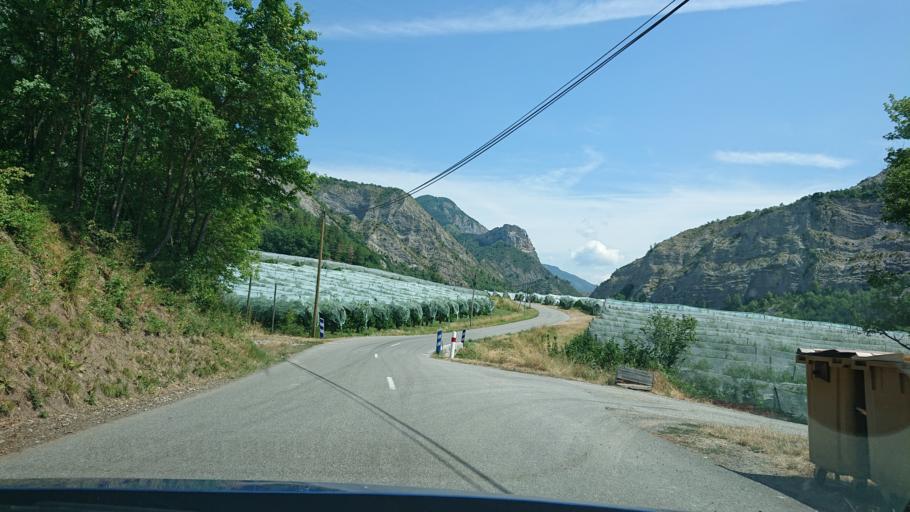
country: FR
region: Provence-Alpes-Cote d'Azur
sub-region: Departement des Hautes-Alpes
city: Tallard
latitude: 44.3594
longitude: 6.0488
